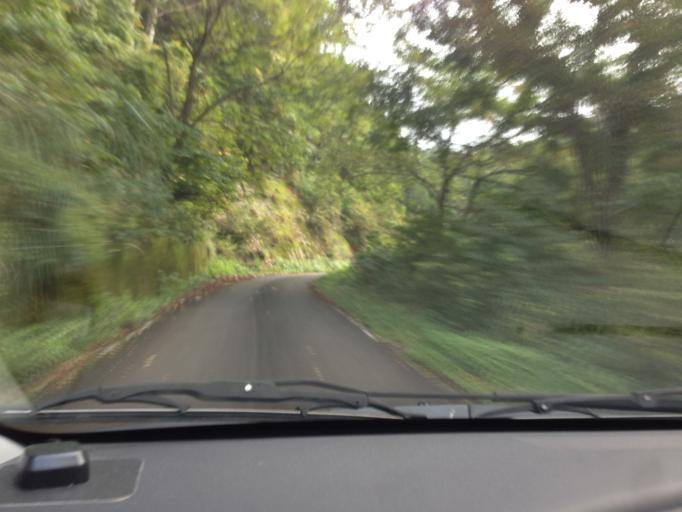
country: JP
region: Fukushima
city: Kitakata
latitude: 37.3854
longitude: 139.6148
